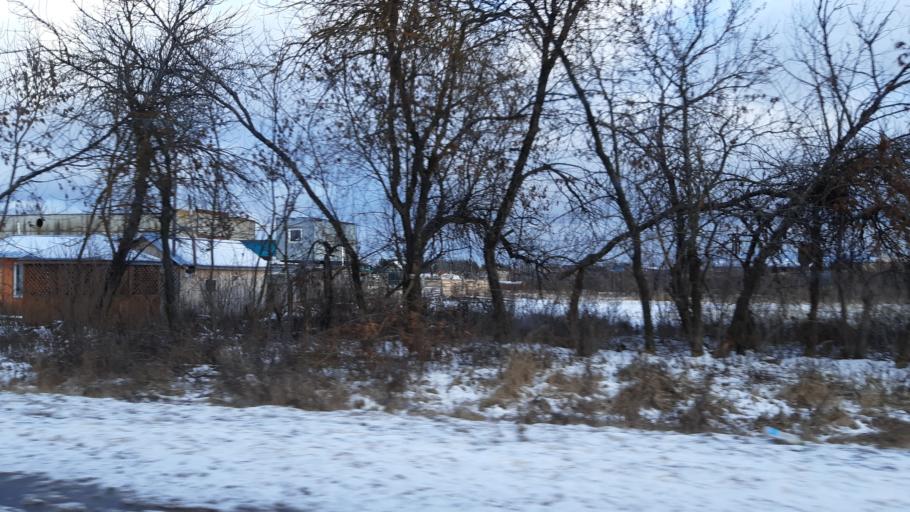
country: RU
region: Moskovskaya
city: Noginsk-9
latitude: 56.0164
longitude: 38.5577
